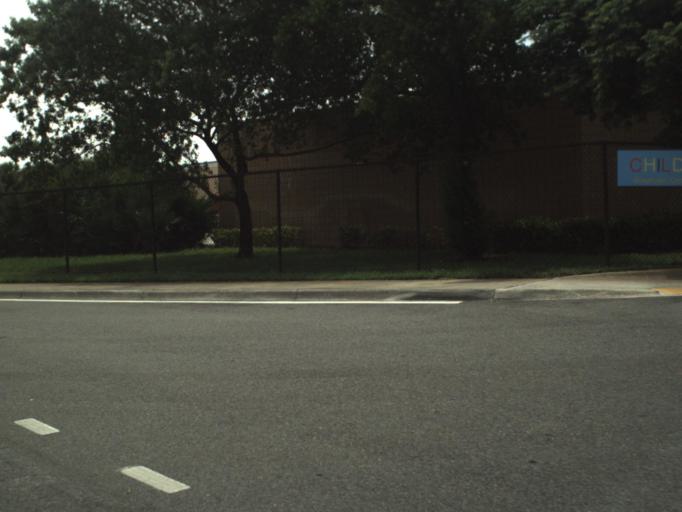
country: US
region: Florida
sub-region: Palm Beach County
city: Mangonia Park
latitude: 26.7812
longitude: -80.0838
